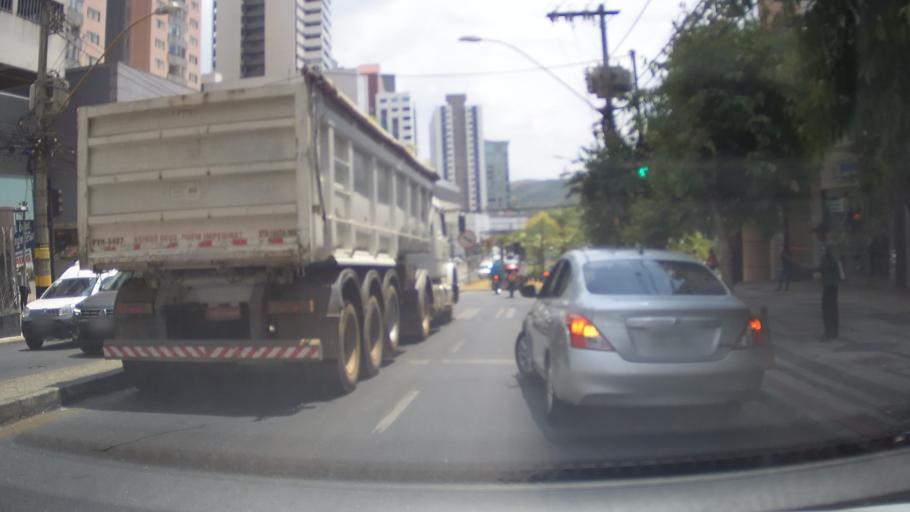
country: BR
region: Minas Gerais
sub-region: Belo Horizonte
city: Belo Horizonte
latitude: -19.9746
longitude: -43.9416
